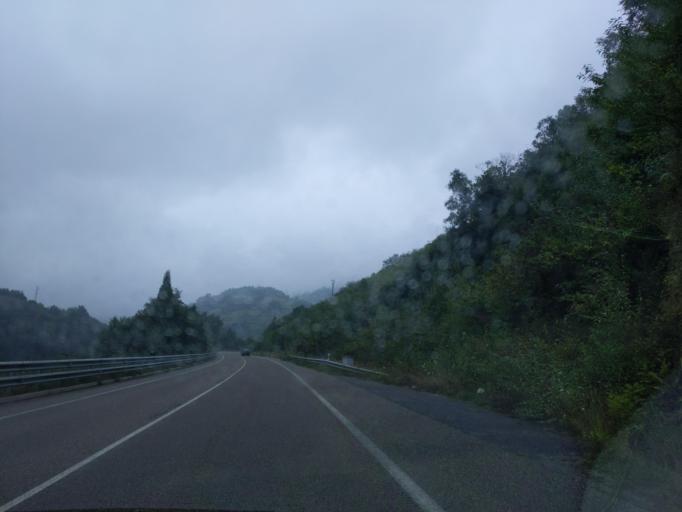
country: ES
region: Asturias
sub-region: Province of Asturias
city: El entrego
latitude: 43.2992
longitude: -5.6059
